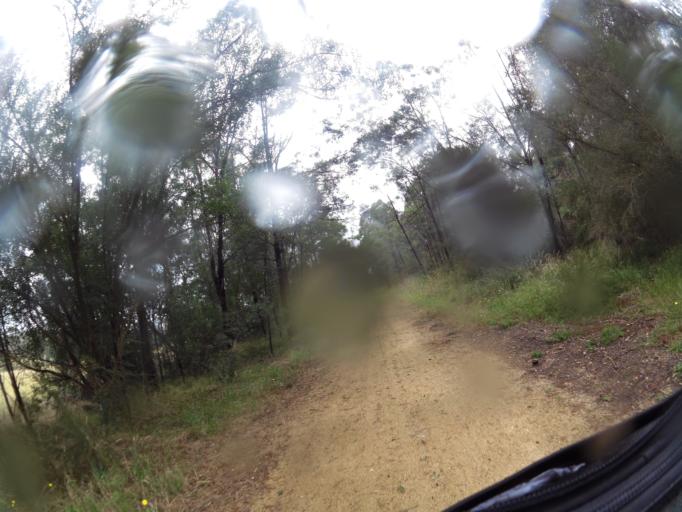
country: AU
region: Victoria
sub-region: East Gippsland
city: Bairnsdale
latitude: -37.7484
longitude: 147.8112
